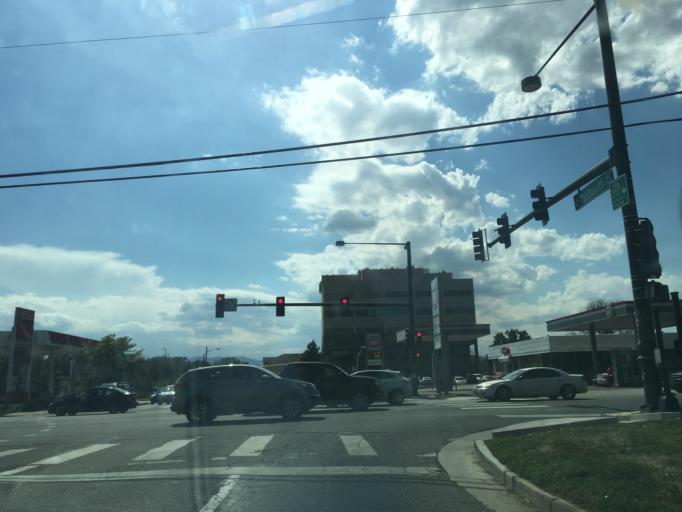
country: US
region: Colorado
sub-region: Arapahoe County
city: Sheridan
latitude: 39.6562
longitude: -105.0529
